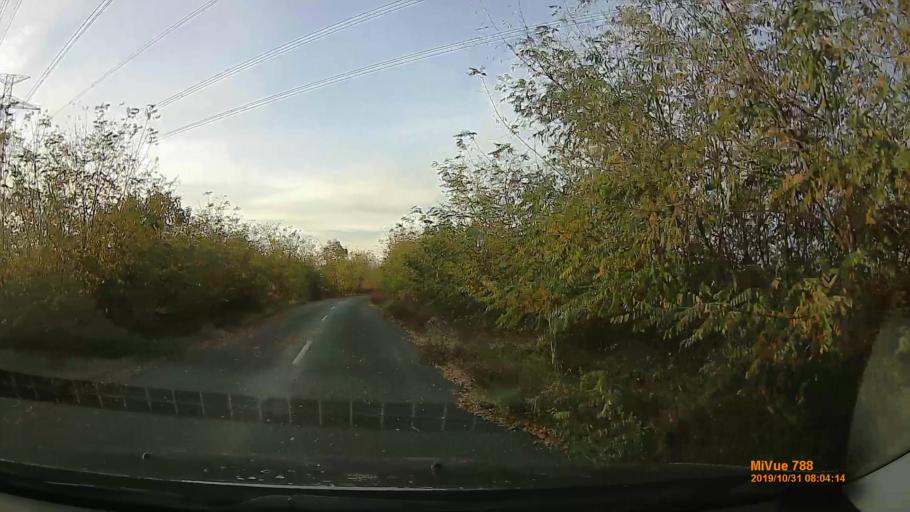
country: HU
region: Pest
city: Pilis
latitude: 47.3145
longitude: 19.5654
